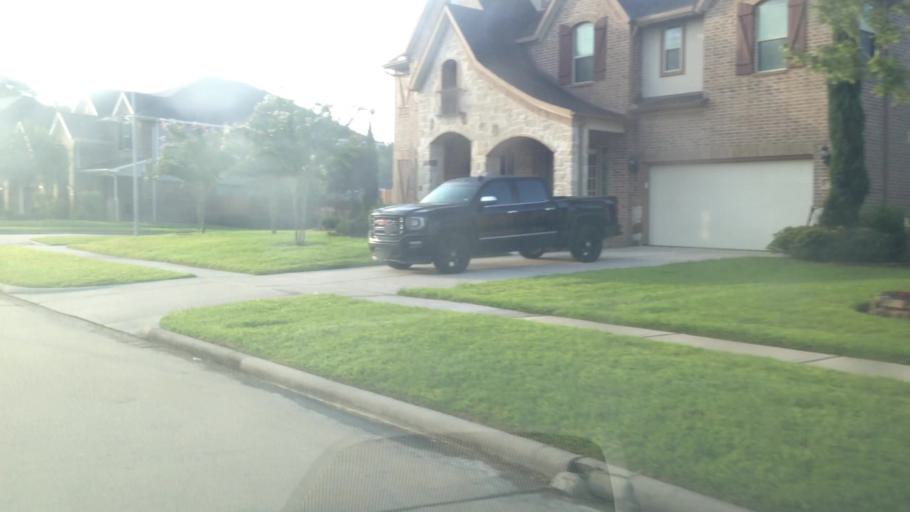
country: US
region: Texas
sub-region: Harris County
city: Sheldon
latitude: 29.9184
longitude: -95.1728
